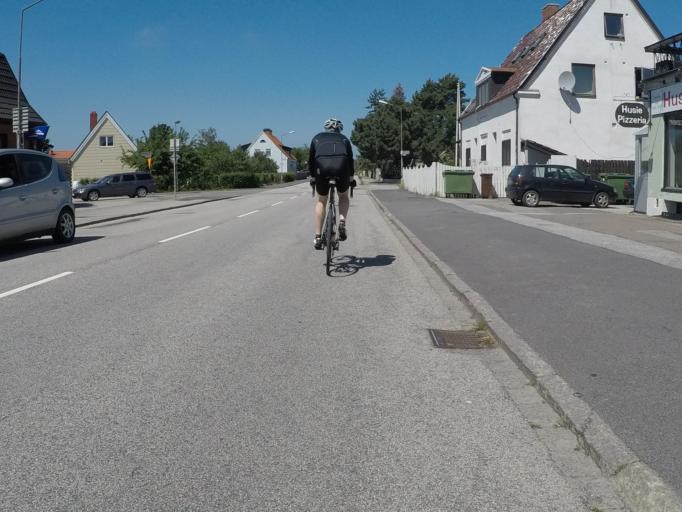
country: SE
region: Skane
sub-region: Burlovs Kommun
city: Arloev
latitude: 55.5903
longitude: 13.0801
